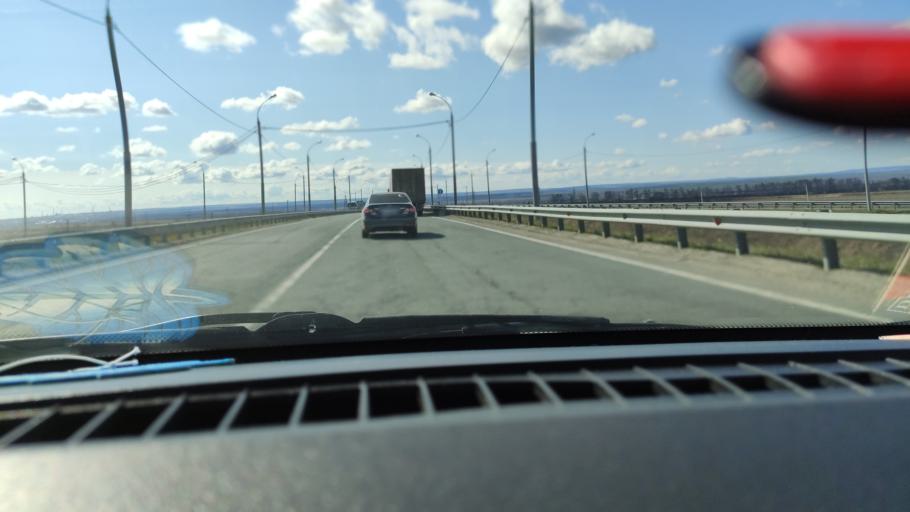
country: RU
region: Samara
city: Varlamovo
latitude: 53.1915
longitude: 48.2922
